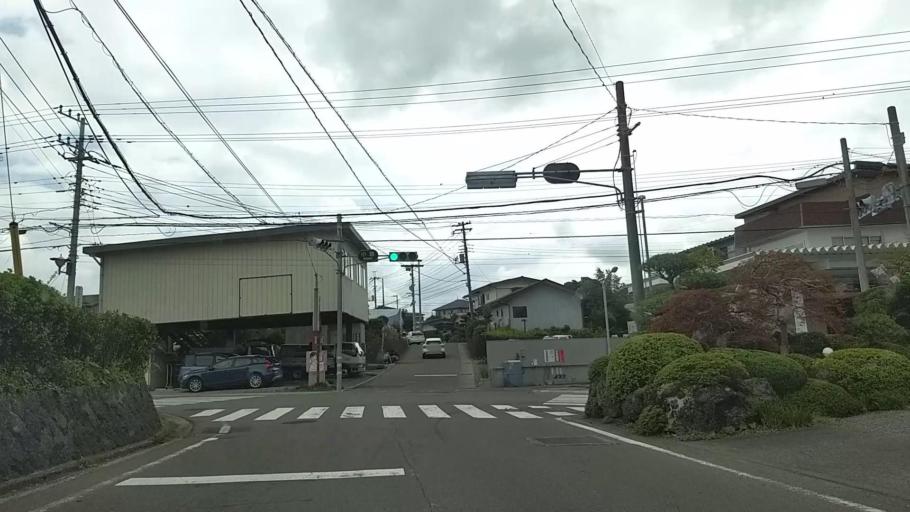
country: JP
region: Yamanashi
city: Fujikawaguchiko
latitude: 35.5036
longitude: 138.7378
